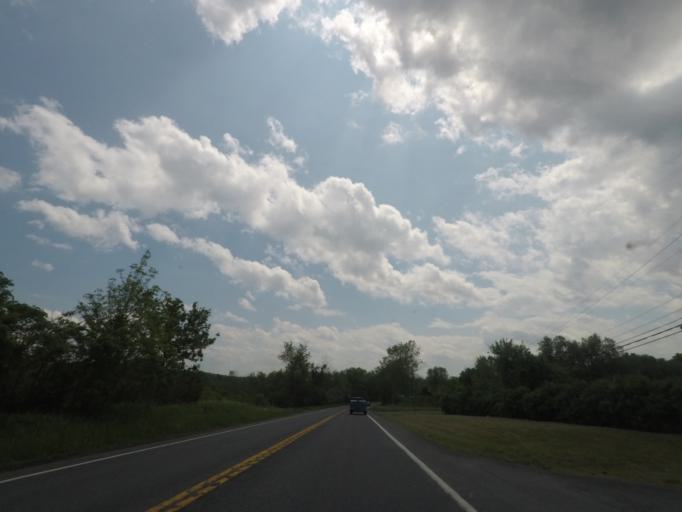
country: US
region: New York
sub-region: Columbia County
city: Stottville
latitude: 42.3107
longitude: -73.7019
